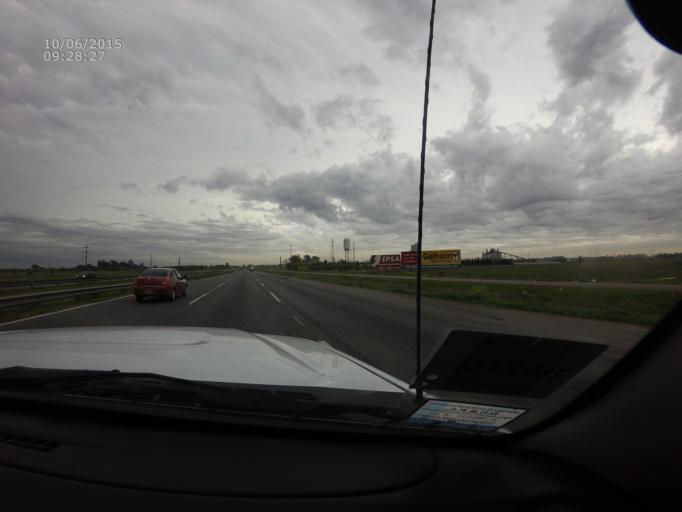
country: AR
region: Buenos Aires
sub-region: Partido de Campana
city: Campana
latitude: -34.1595
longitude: -59.0124
